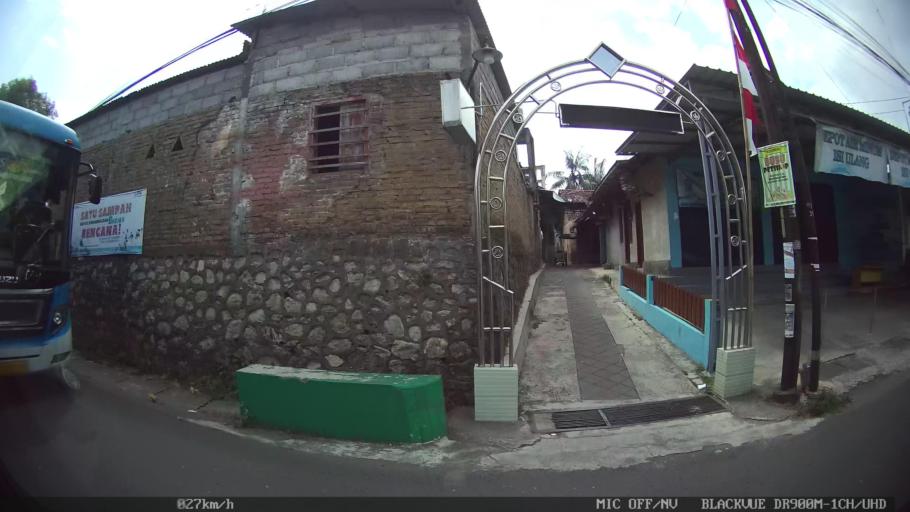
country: ID
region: Daerah Istimewa Yogyakarta
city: Kasihan
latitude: -7.8143
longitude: 110.3337
